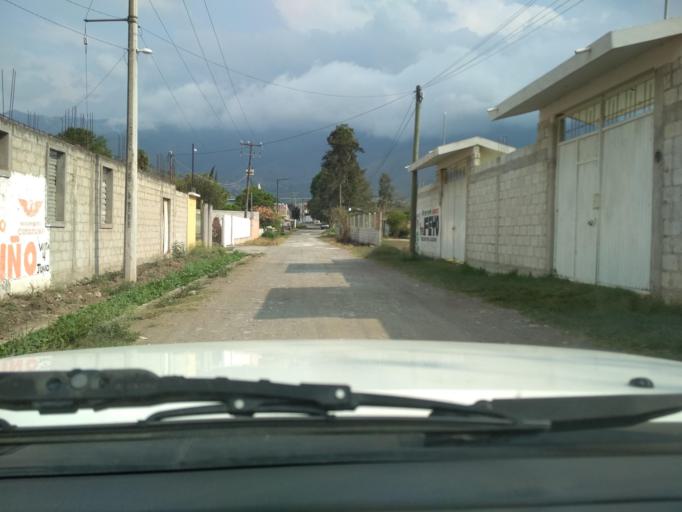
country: MX
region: Veracruz
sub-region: Acultzingo
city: Acatla
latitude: 18.7665
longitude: -97.2245
